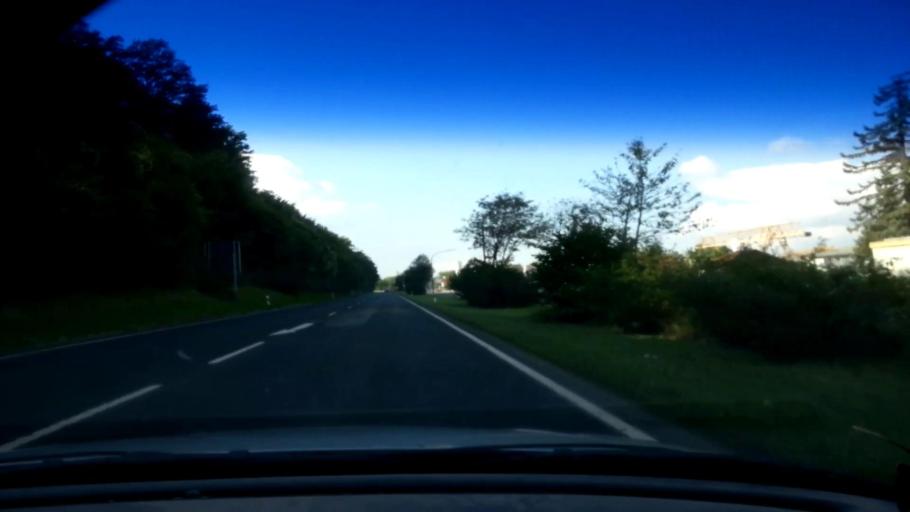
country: DE
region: Bavaria
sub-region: Upper Franconia
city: Oberhaid
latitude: 49.9191
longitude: 10.8032
